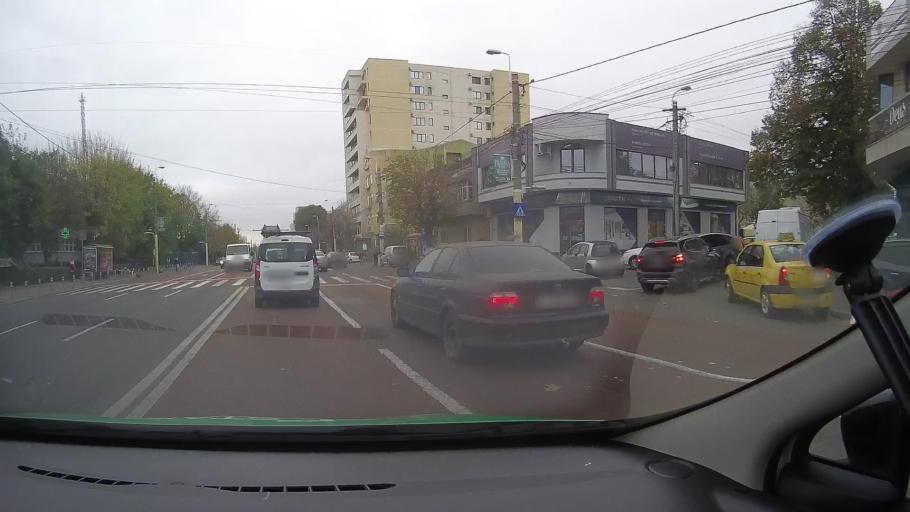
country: RO
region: Constanta
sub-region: Municipiul Constanta
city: Constanta
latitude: 44.1722
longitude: 28.6305
